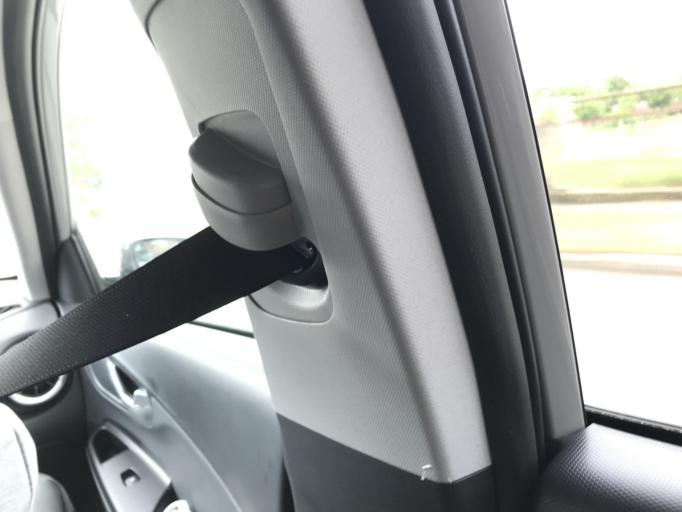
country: GE
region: Kvemo Kartli
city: Rust'avi
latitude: 41.5511
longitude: 44.9803
